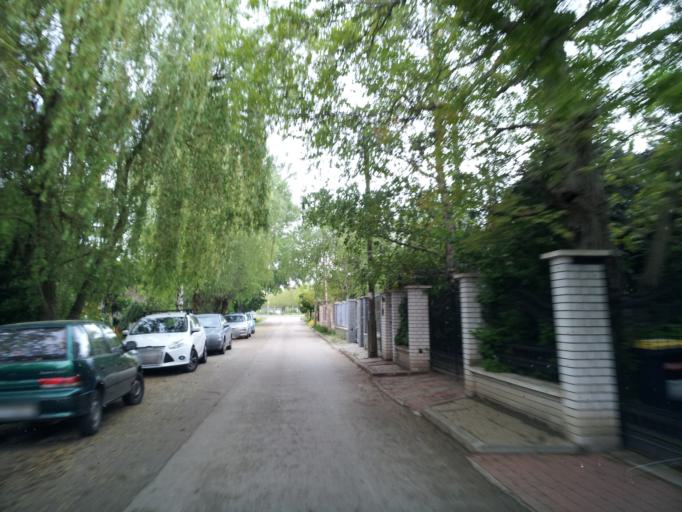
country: HU
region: Budapest
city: Budapest XXII. keruelet
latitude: 47.4438
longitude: 19.0144
